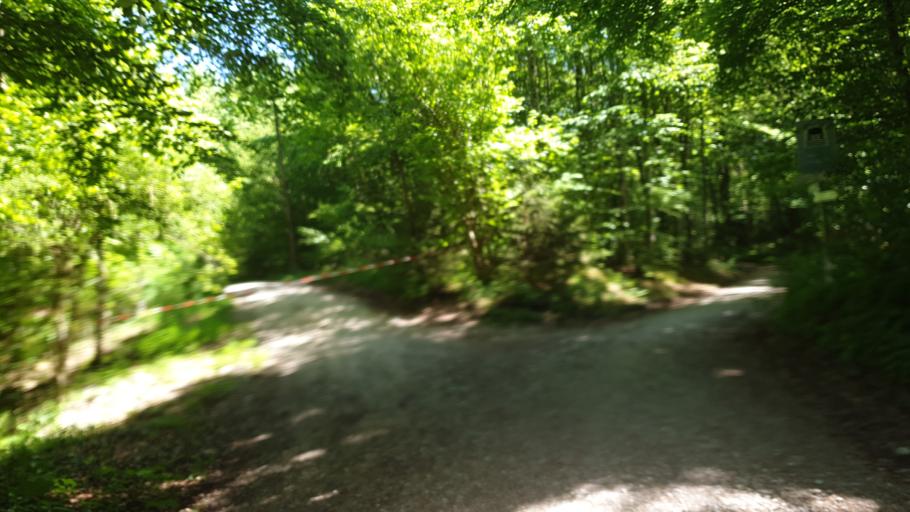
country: DE
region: Bavaria
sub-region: Upper Bavaria
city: Seeshaupt
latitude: 47.8056
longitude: 11.2862
